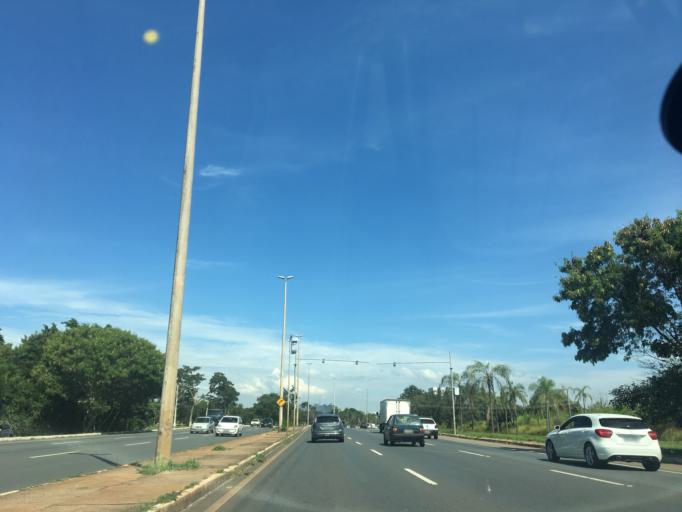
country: BR
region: Federal District
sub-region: Brasilia
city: Brasilia
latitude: -15.8075
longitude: -47.8513
